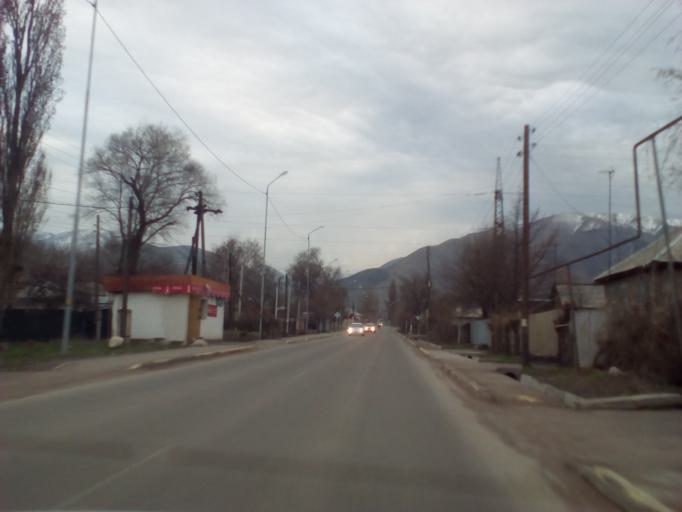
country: KZ
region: Almaty Oblysy
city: Burunday
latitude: 43.1703
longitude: 76.4161
